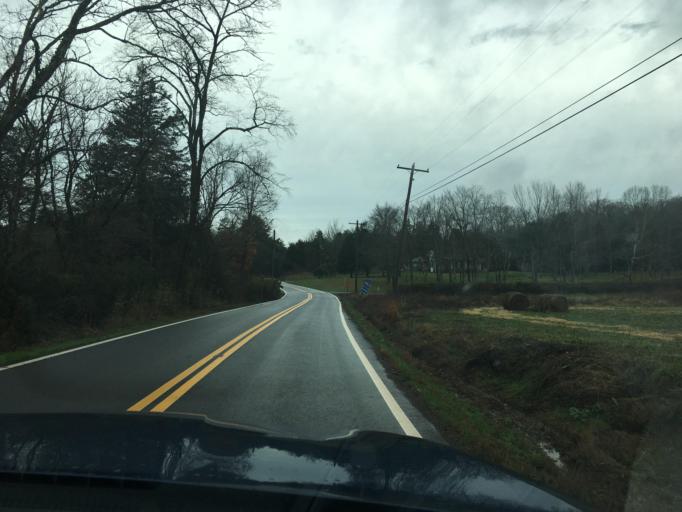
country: US
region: Tennessee
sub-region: McMinn County
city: Englewood
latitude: 35.4051
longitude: -84.4525
